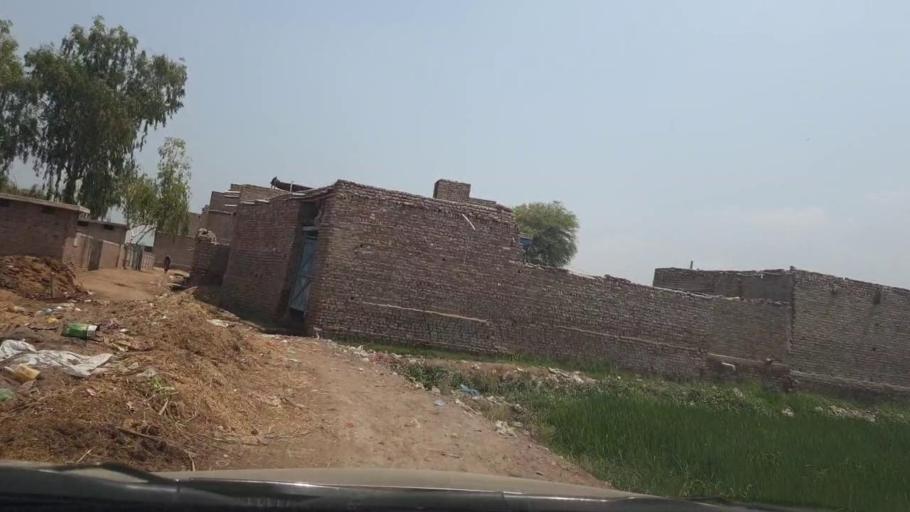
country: PK
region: Sindh
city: Ratodero
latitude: 27.7296
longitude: 68.2954
